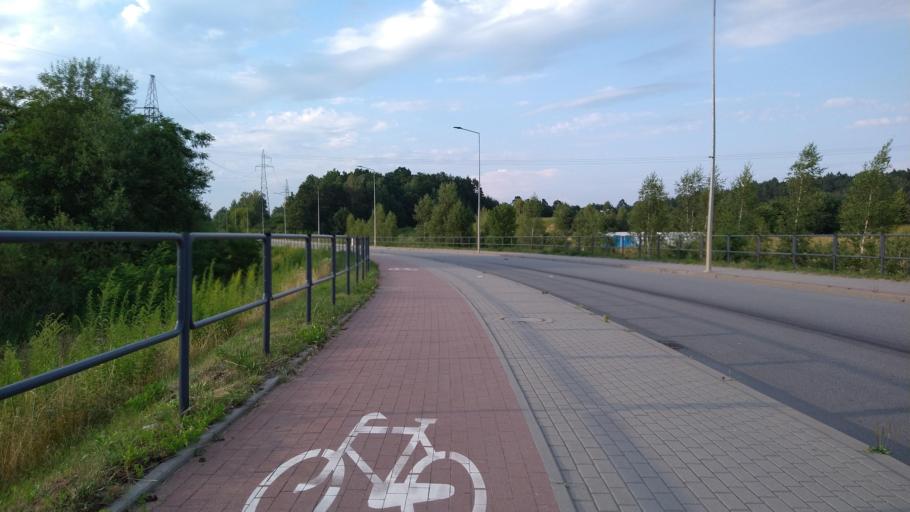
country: PL
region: Warmian-Masurian Voivodeship
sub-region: Powiat olsztynski
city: Olsztyn
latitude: 53.7818
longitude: 20.5509
